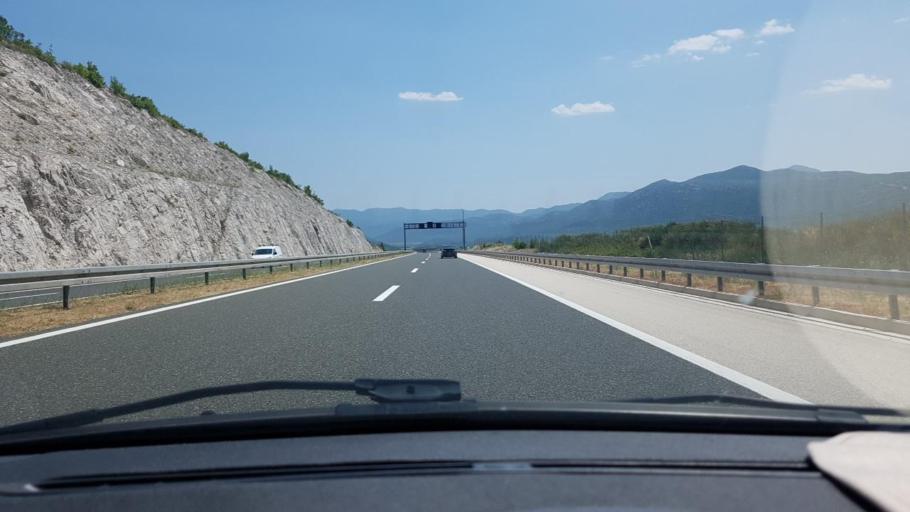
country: HR
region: Splitsko-Dalmatinska
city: Runovic
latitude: 43.2956
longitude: 17.1951
